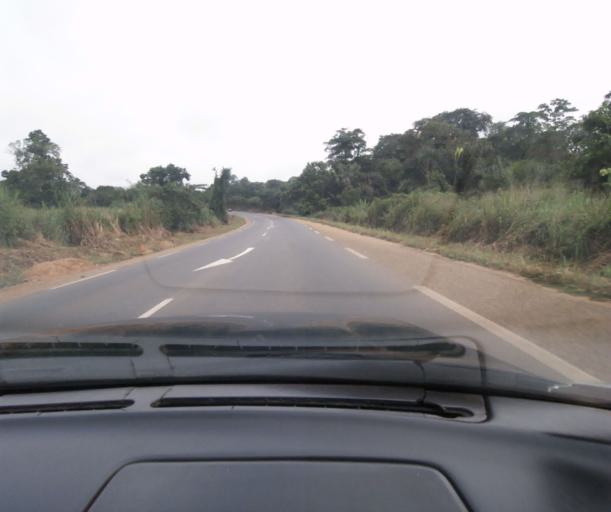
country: CM
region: Centre
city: Obala
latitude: 4.0922
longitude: 11.5427
